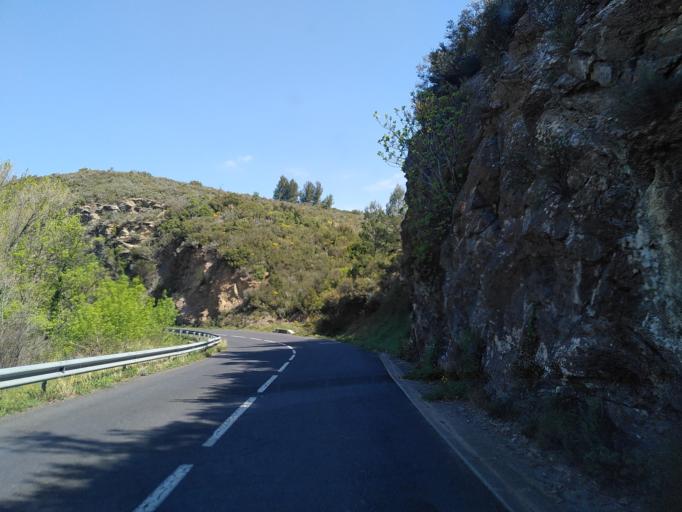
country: FR
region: Languedoc-Roussillon
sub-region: Departement de l'Aude
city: Portel-des-Corbieres
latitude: 42.9893
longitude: 2.7898
